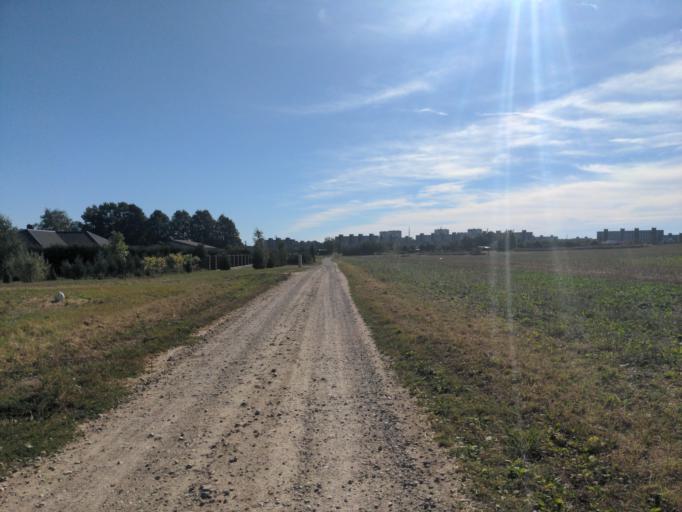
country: LT
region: Siauliu apskritis
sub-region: Siauliai
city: Siauliai
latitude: 55.9227
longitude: 23.2453
